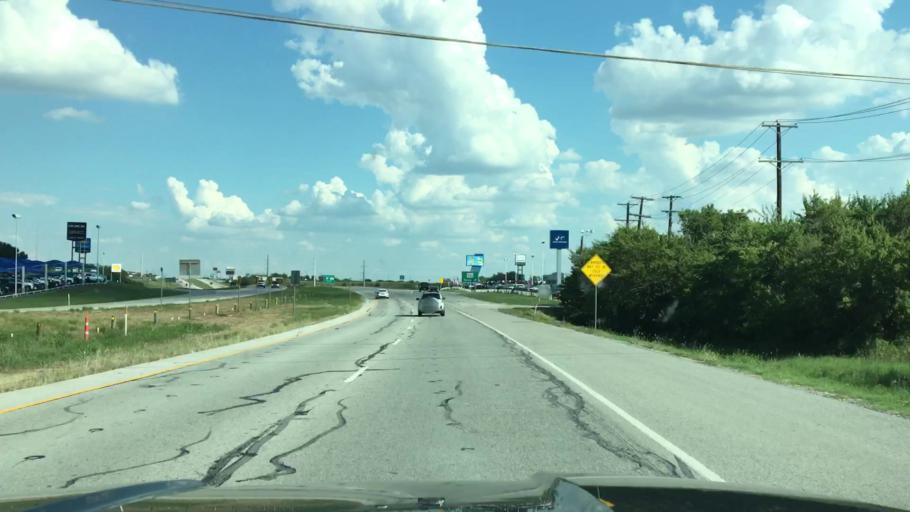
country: US
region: Texas
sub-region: Wise County
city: Decatur
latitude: 33.2172
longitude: -97.5873
